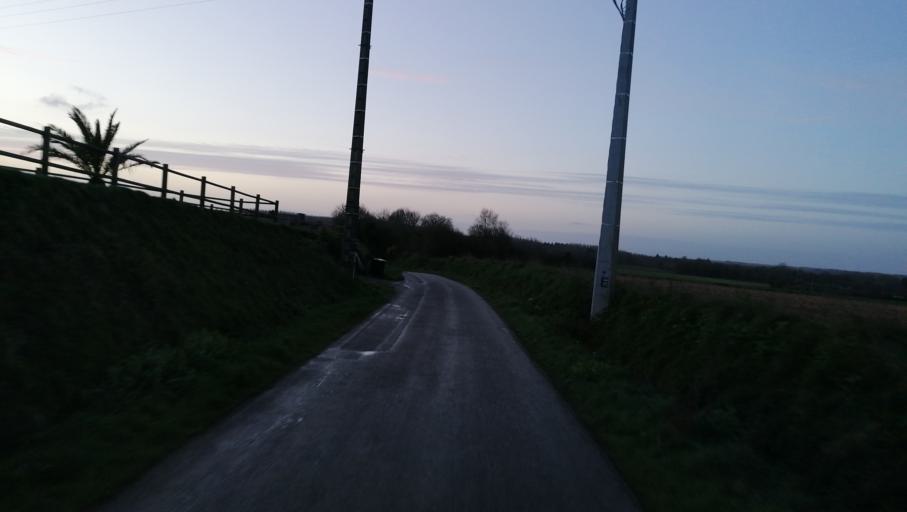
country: FR
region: Brittany
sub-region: Departement des Cotes-d'Armor
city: Plouha
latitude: 48.6690
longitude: -2.9596
